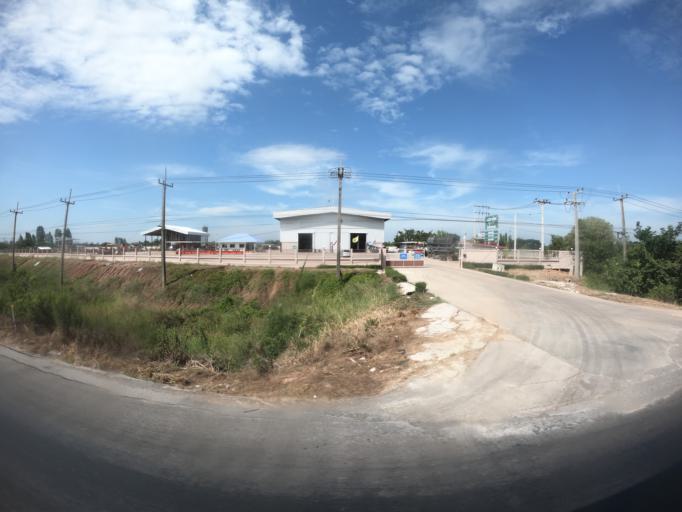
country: TH
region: Khon Kaen
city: Khon Kaen
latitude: 16.4215
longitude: 102.9169
